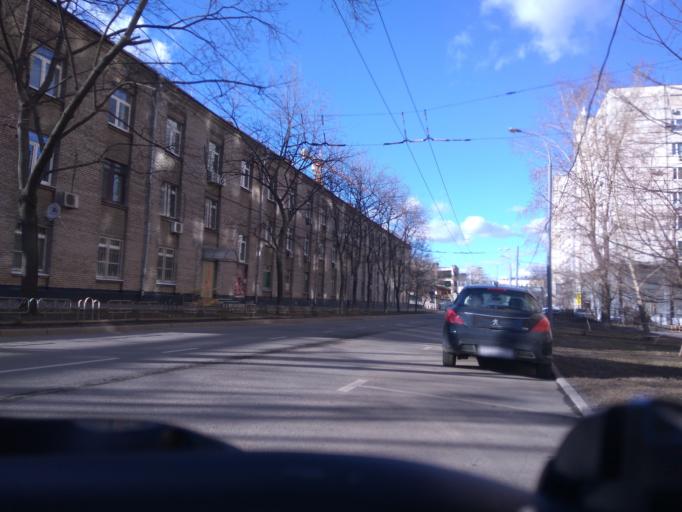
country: RU
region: Moscow
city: Mar'ina Roshcha
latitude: 55.8111
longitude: 37.6314
